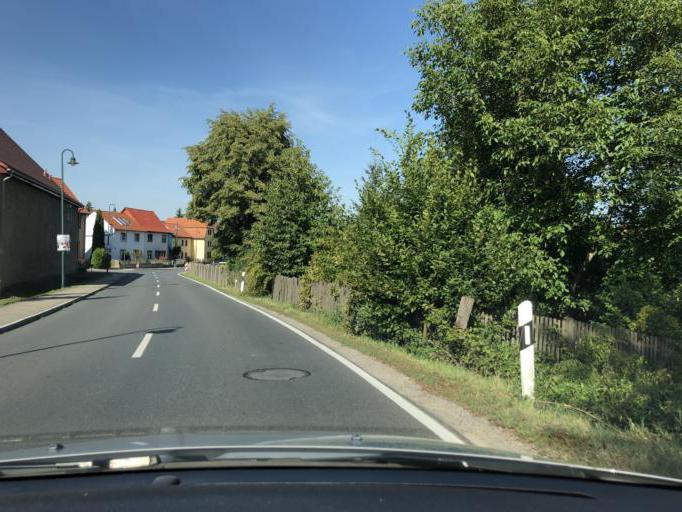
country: DE
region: Saxony-Anhalt
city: Bad Bibra
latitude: 51.2039
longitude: 11.5822
